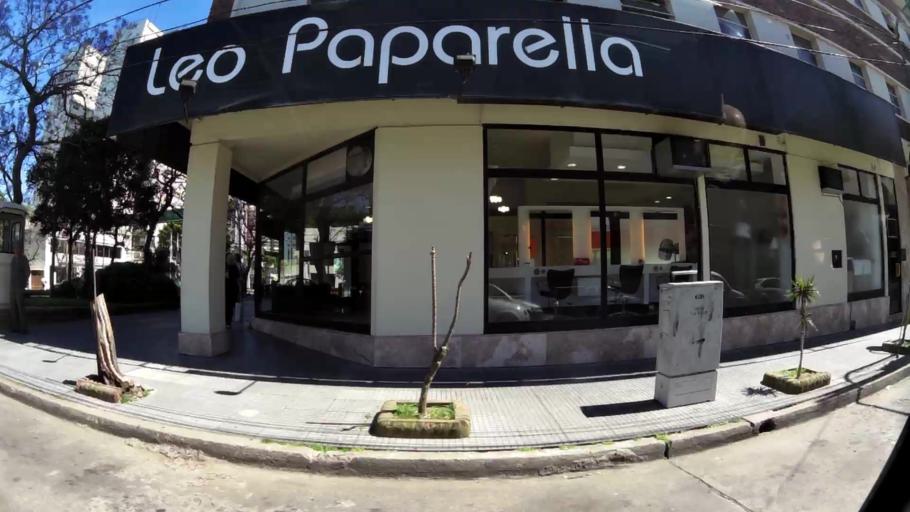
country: AR
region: Buenos Aires
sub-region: Partido de Vicente Lopez
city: Olivos
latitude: -34.5097
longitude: -58.4786
